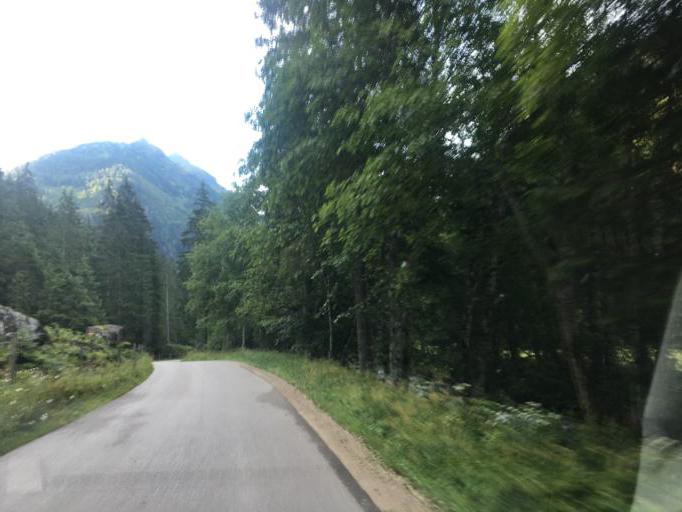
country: AT
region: Styria
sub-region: Politischer Bezirk Liezen
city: Haus
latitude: 47.3327
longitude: 13.7520
